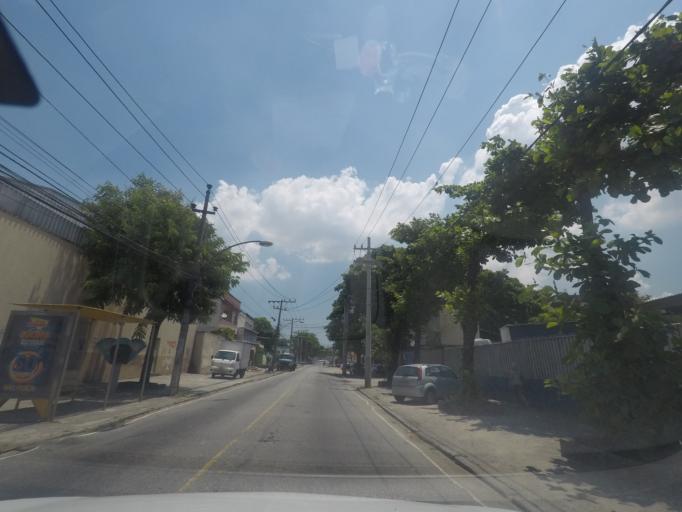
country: BR
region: Rio de Janeiro
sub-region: Duque De Caxias
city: Duque de Caxias
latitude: -22.8222
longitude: -43.3075
